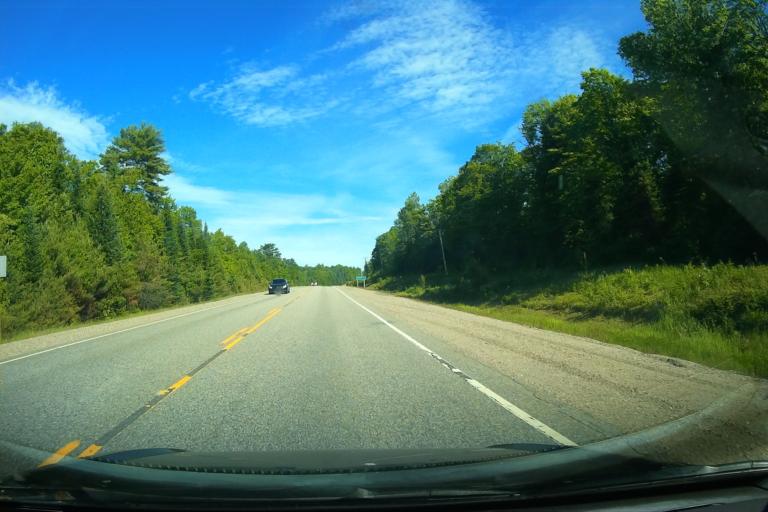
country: CA
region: Ontario
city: Deep River
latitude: 46.1547
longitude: -77.5887
